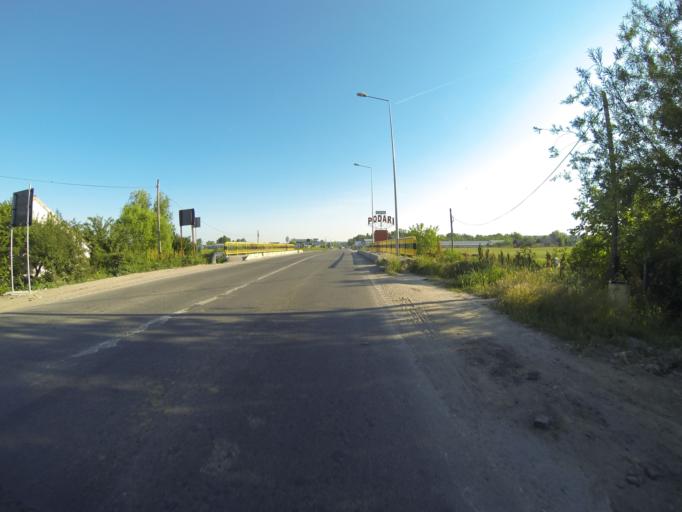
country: RO
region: Dolj
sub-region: Municipiul Craiova
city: Popoveni
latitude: 44.2836
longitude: 23.7977
